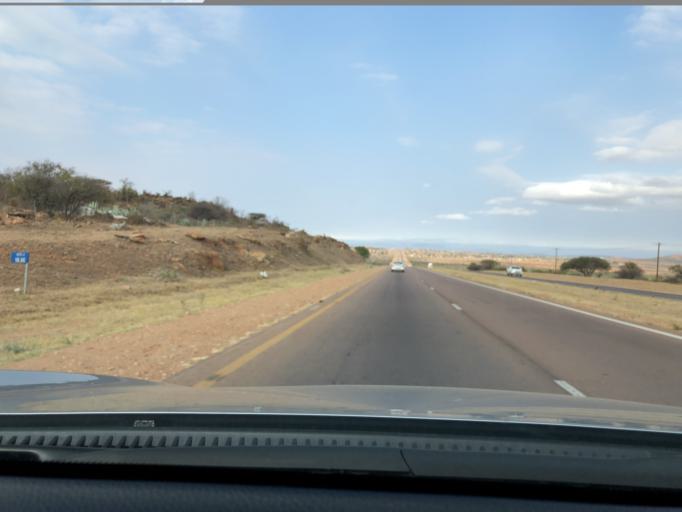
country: ZA
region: Limpopo
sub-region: Capricorn District Municipality
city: Polokwane
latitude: -23.8973
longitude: 29.6210
